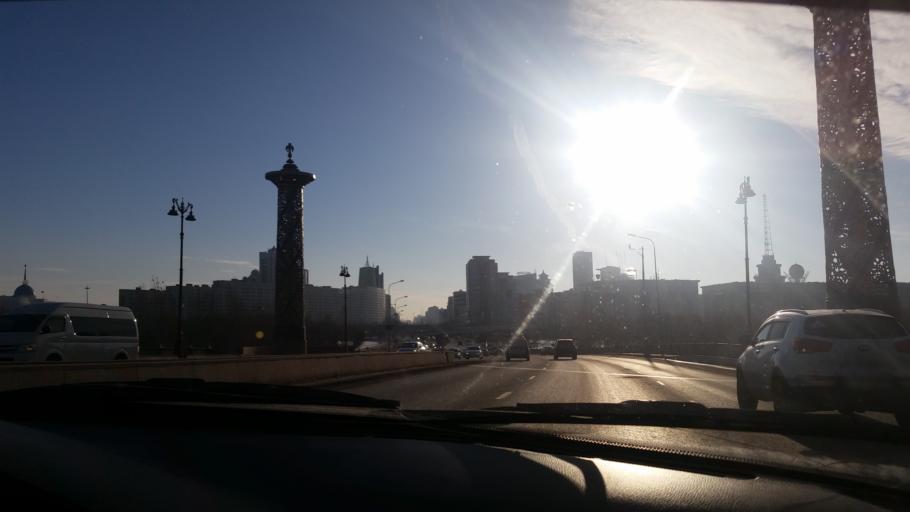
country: KZ
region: Astana Qalasy
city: Astana
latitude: 51.1369
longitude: 71.4424
